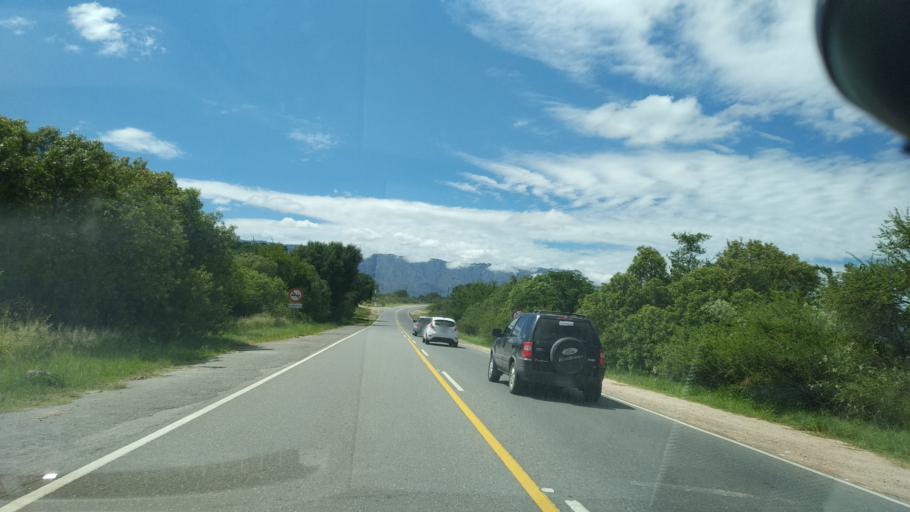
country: AR
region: Cordoba
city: Mina Clavero
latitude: -31.7574
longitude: -64.9740
